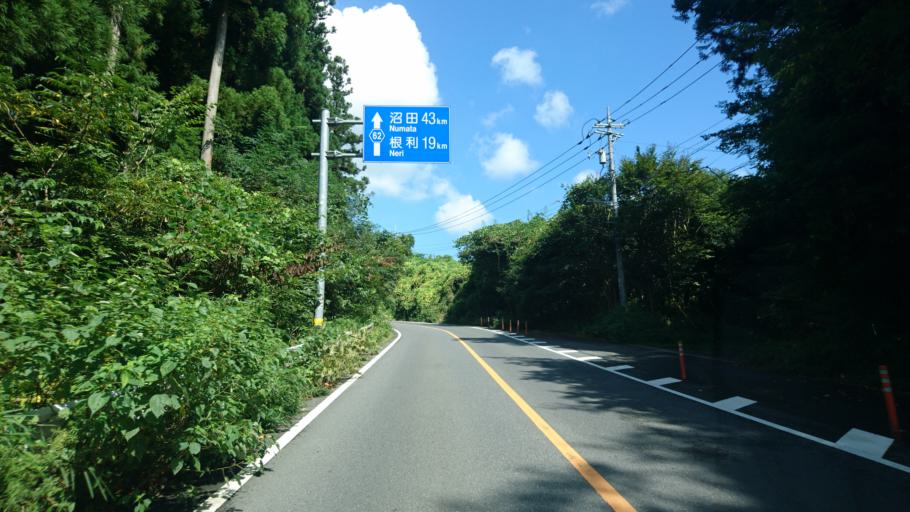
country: JP
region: Gunma
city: Omamacho-omama
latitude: 36.4927
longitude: 139.2725
